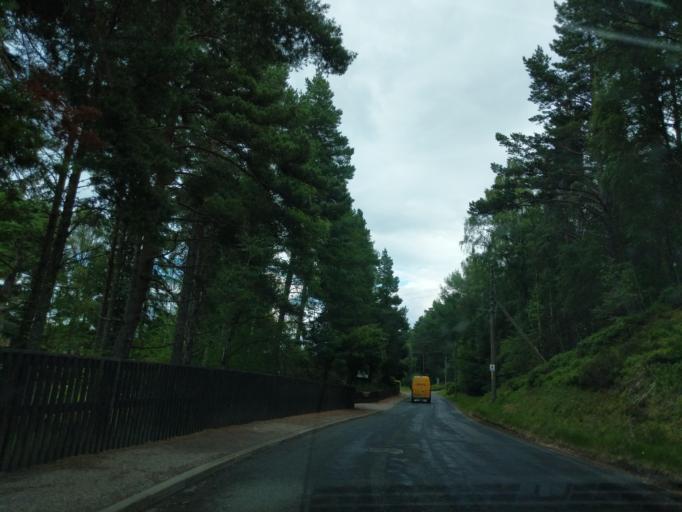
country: GB
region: Scotland
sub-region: Highland
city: Aviemore
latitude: 57.2832
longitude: -3.8219
